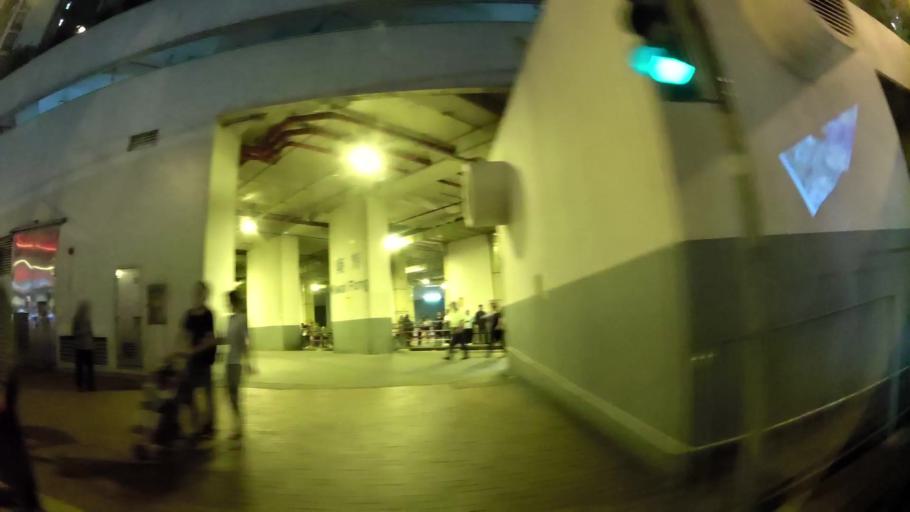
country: HK
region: Tsuen Wan
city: Tsuen Wan
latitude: 22.3563
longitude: 114.1281
